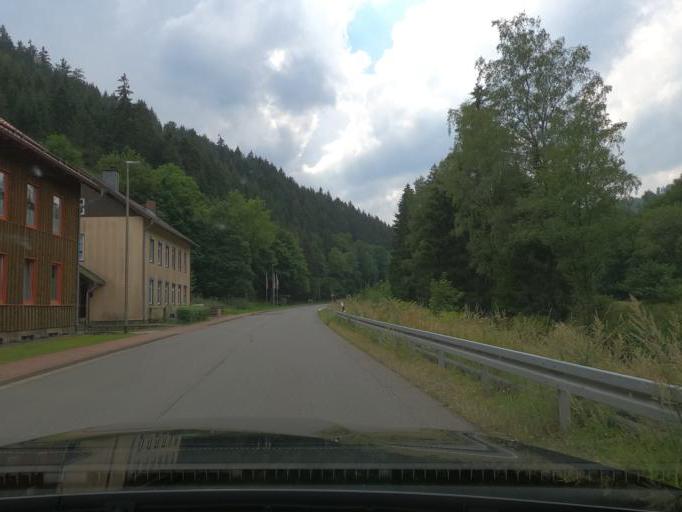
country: DE
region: Lower Saxony
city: Wildemann
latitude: 51.8624
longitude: 10.2808
